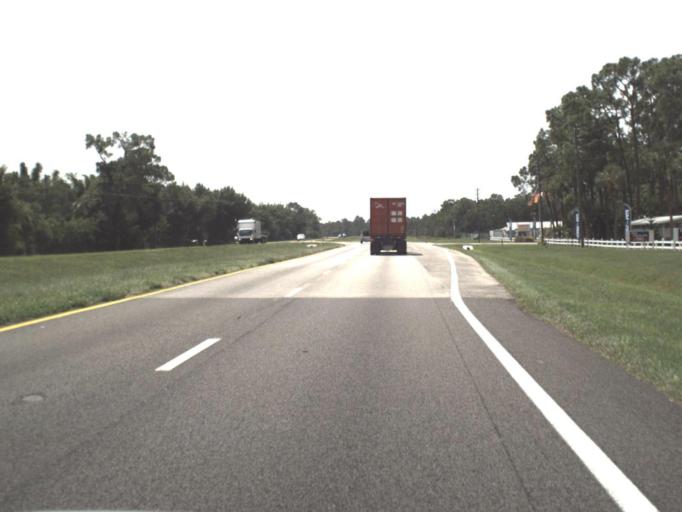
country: US
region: Florida
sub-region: Polk County
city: Crooked Lake Park
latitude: 27.7773
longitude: -81.5974
